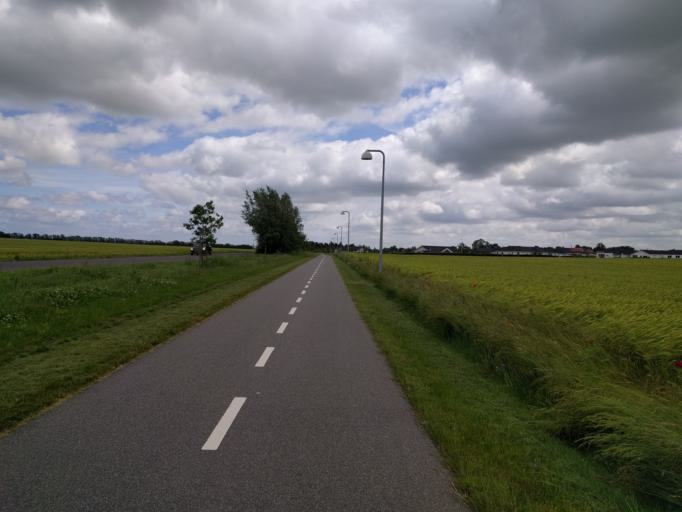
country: DK
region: South Denmark
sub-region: Odense Kommune
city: Seden
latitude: 55.4109
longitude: 10.4565
